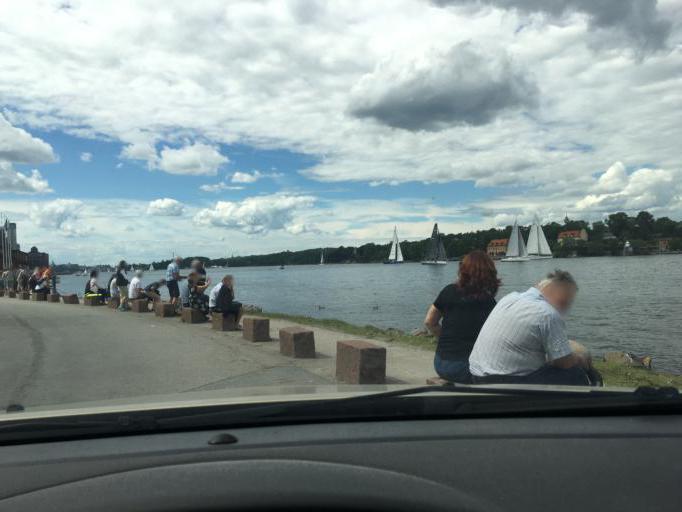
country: SE
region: Stockholm
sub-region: Nacka Kommun
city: Nacka
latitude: 59.3181
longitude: 18.1591
